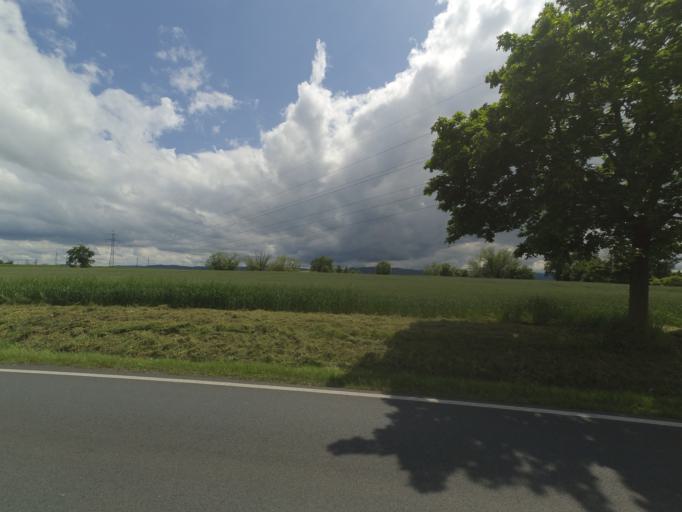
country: CZ
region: Plzensky
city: Klatovy
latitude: 49.3910
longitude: 13.2667
